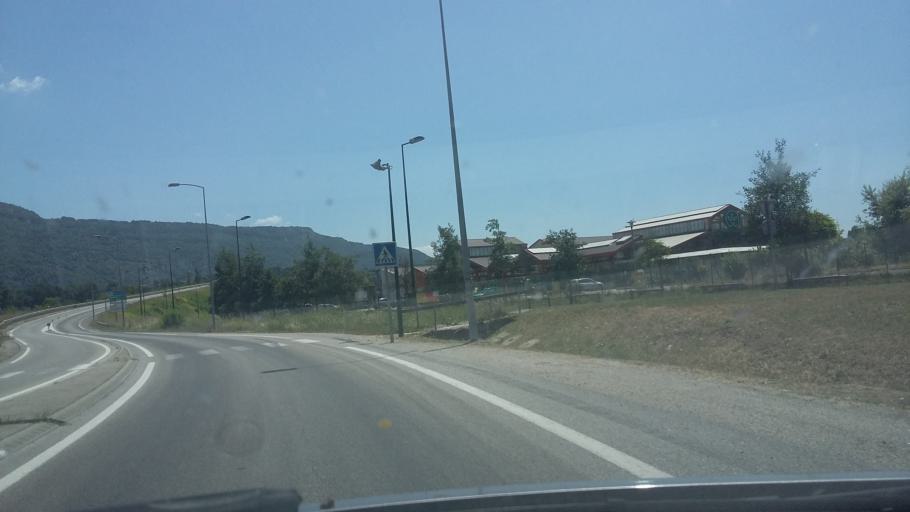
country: FR
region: Rhone-Alpes
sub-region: Departement de l'Ain
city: Belley
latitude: 45.7577
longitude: 5.7055
